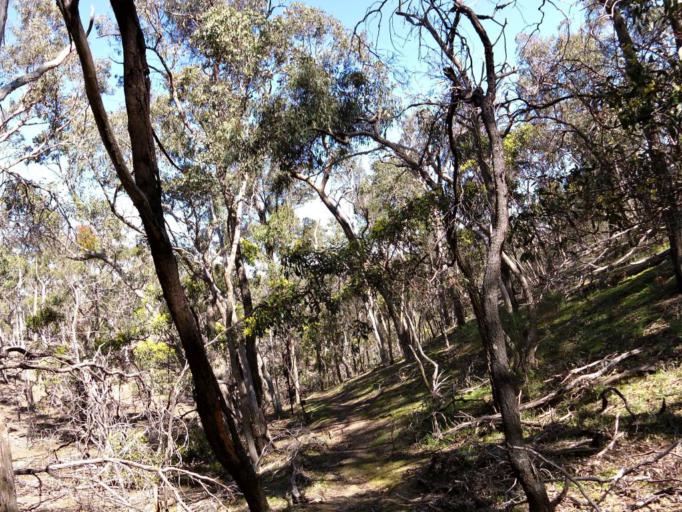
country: AU
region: Victoria
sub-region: Moorabool
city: Bacchus Marsh
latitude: -37.6705
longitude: 144.3191
